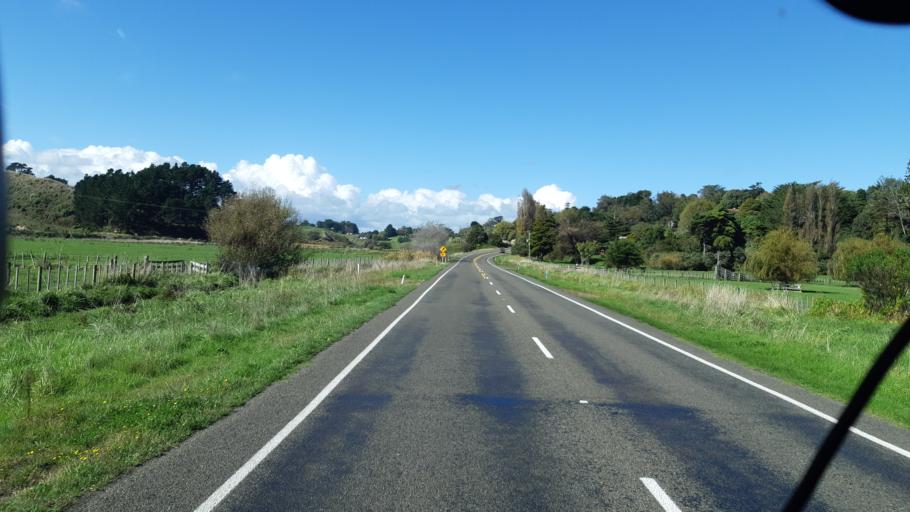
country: NZ
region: Manawatu-Wanganui
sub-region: Wanganui District
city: Wanganui
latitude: -39.9530
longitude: 175.0618
